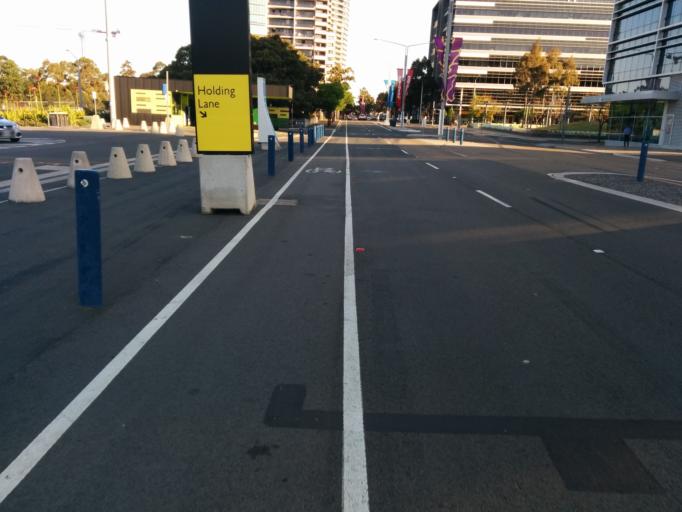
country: AU
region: New South Wales
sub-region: Canada Bay
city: Concord West
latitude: -33.8448
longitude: 151.0713
